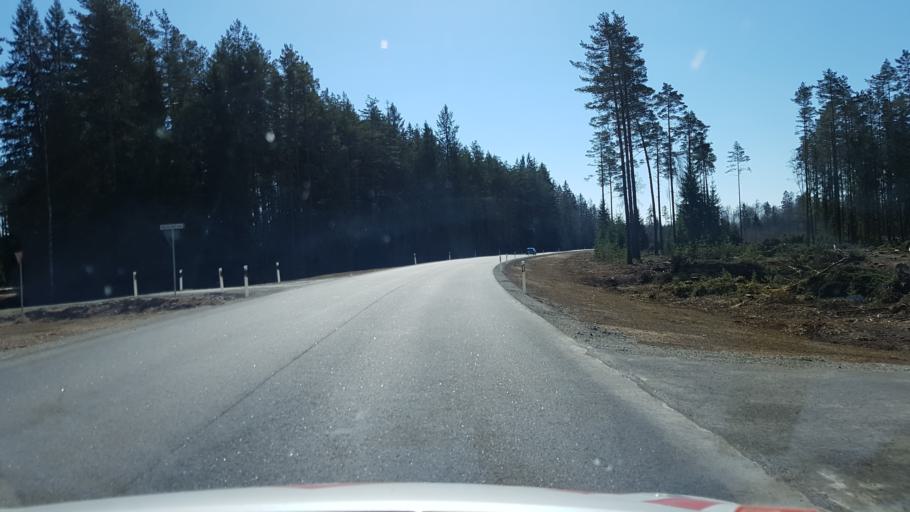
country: EE
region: Laeaene-Virumaa
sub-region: Vinni vald
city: Vinni
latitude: 59.1254
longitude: 26.6157
